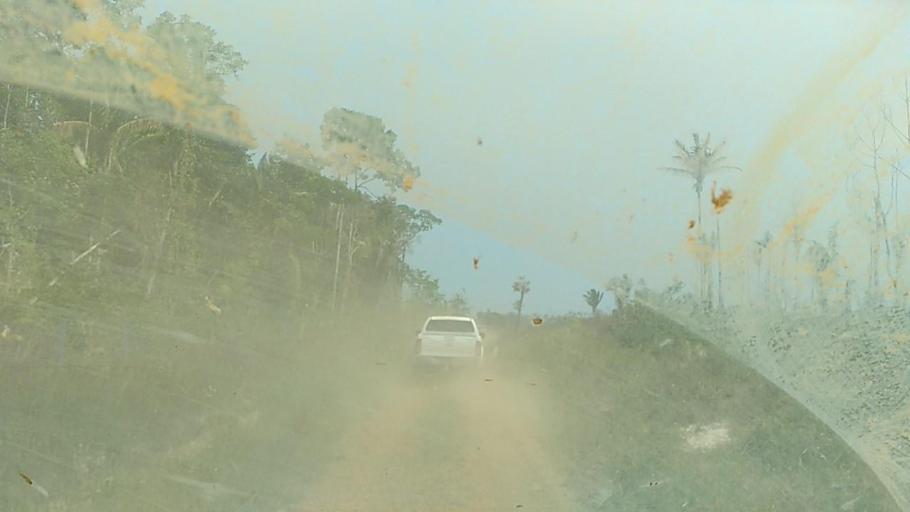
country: BR
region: Rondonia
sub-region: Porto Velho
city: Porto Velho
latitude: -8.9657
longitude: -64.3943
